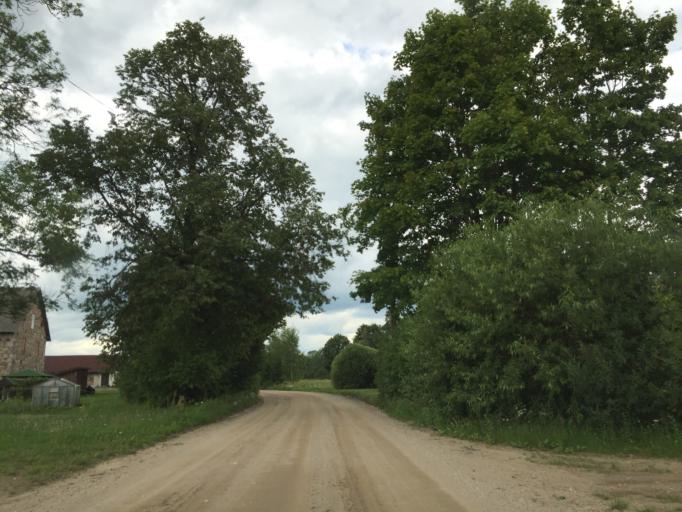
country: LV
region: Malpils
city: Malpils
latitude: 56.8825
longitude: 24.9840
